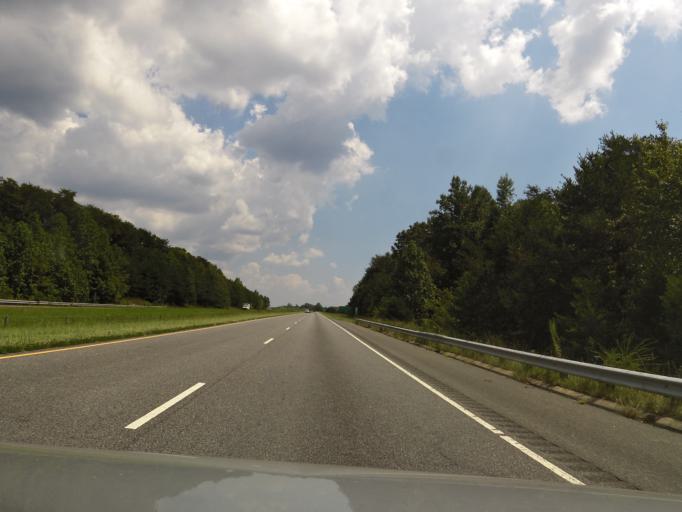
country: US
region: North Carolina
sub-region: Polk County
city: Columbus
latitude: 35.2888
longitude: -82.0796
